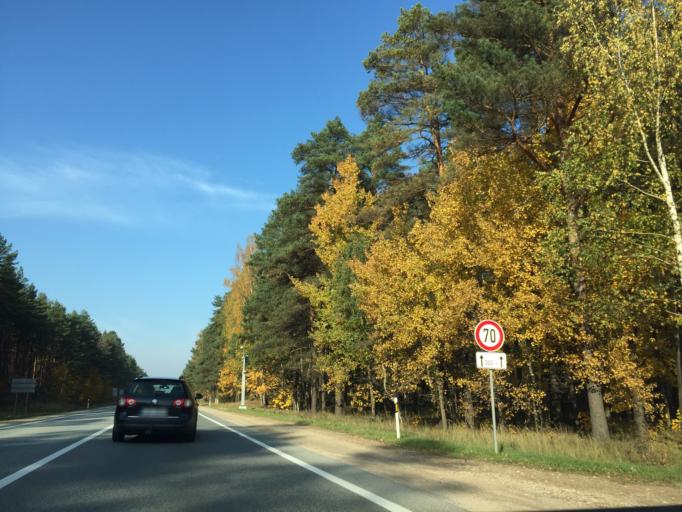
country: LV
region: Babite
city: Pinki
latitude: 56.8861
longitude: 23.9428
